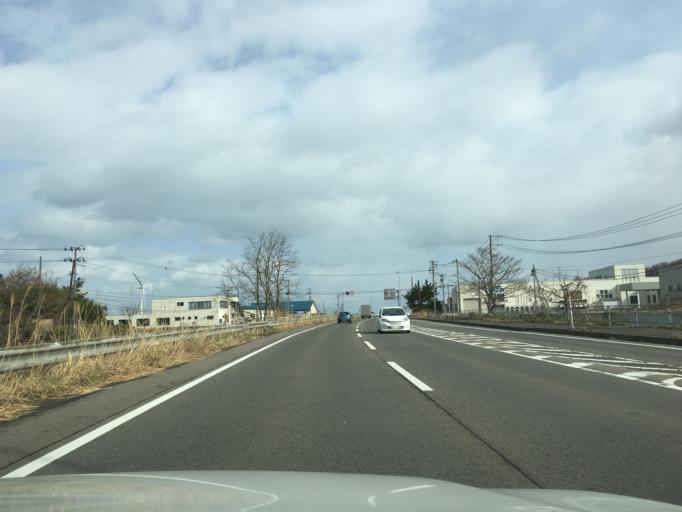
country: JP
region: Yamagata
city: Yuza
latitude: 39.2671
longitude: 139.9228
